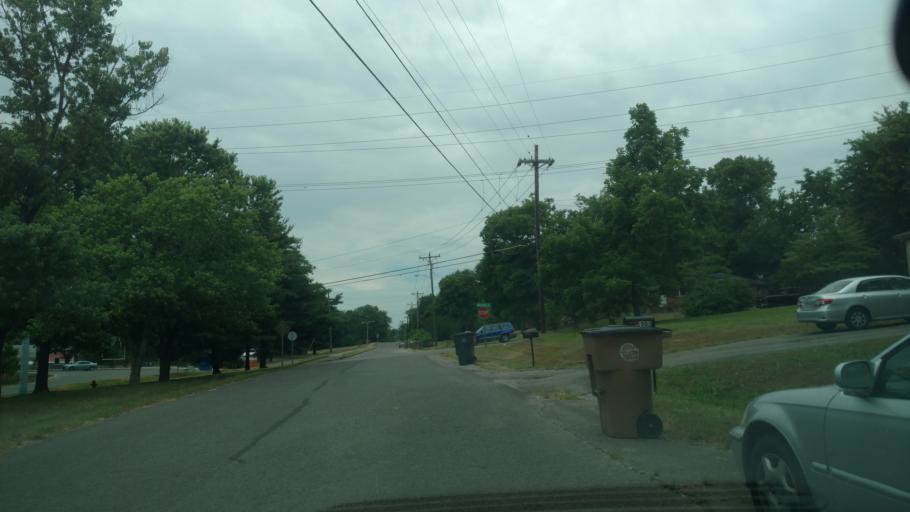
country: US
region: Tennessee
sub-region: Davidson County
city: Nashville
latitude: 36.2003
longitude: -86.7159
